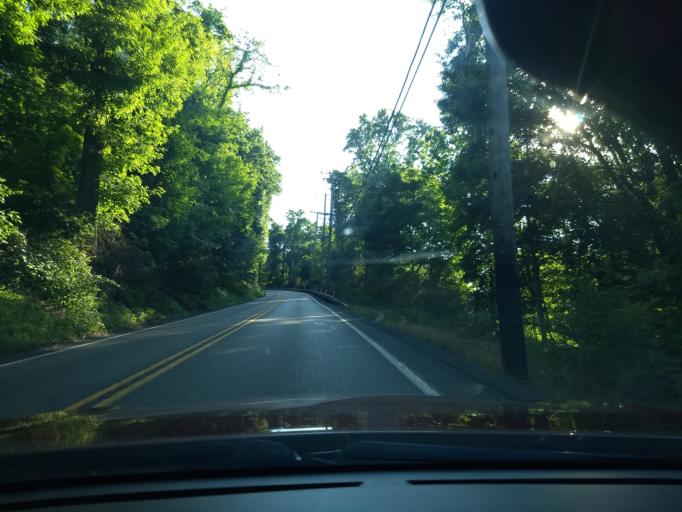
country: US
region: Pennsylvania
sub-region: Allegheny County
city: Churchill
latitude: 40.4487
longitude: -79.8472
